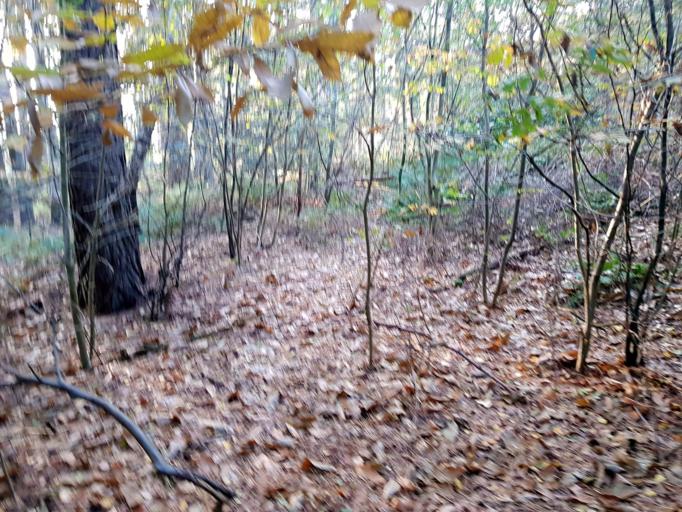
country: NL
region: Utrecht
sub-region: Gemeente Utrechtse Heuvelrug
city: Leersum
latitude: 52.0242
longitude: 5.4085
